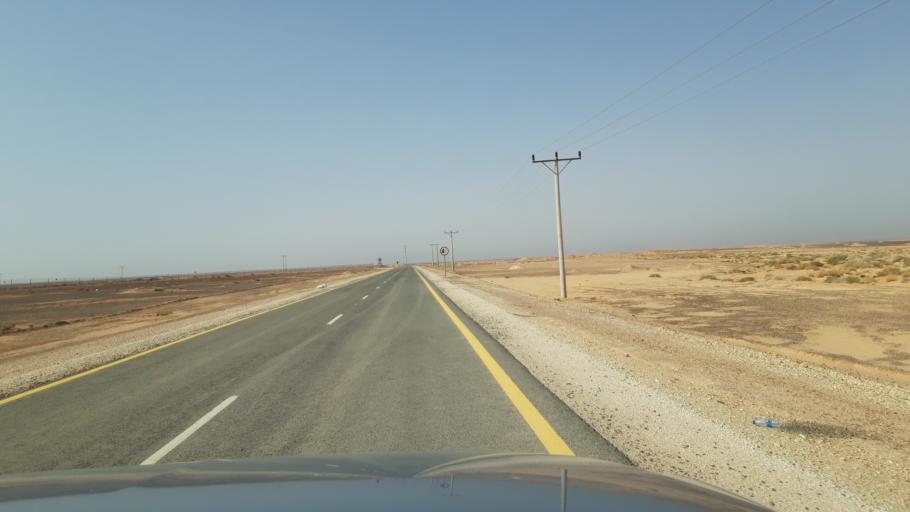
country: JO
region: Amman
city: Al Azraq ash Shamali
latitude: 31.7629
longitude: 36.7548
